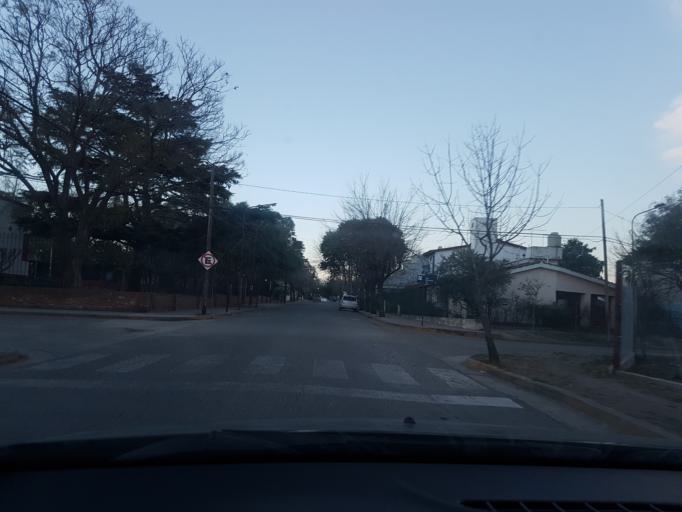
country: AR
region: Cordoba
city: Villa Allende
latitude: -31.2909
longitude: -64.2981
